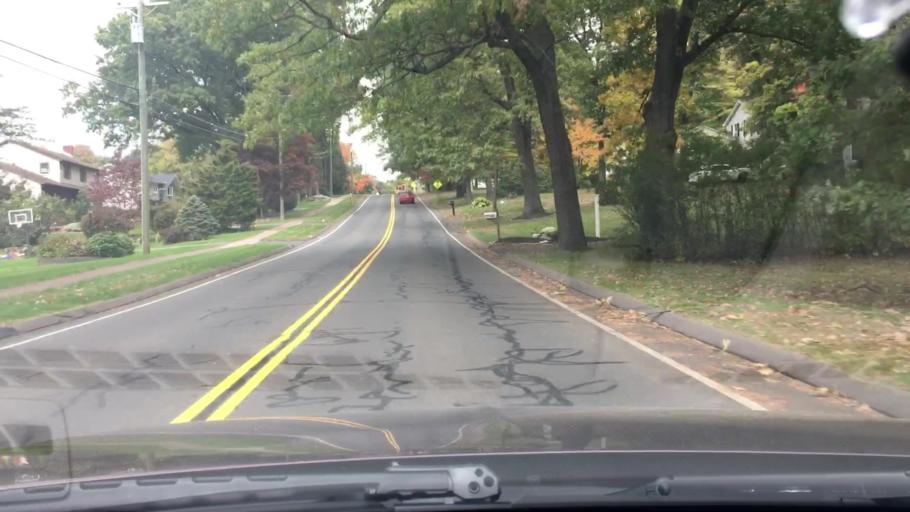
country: US
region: Connecticut
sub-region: Hartford County
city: Manchester
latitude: 41.8248
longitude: -72.5311
